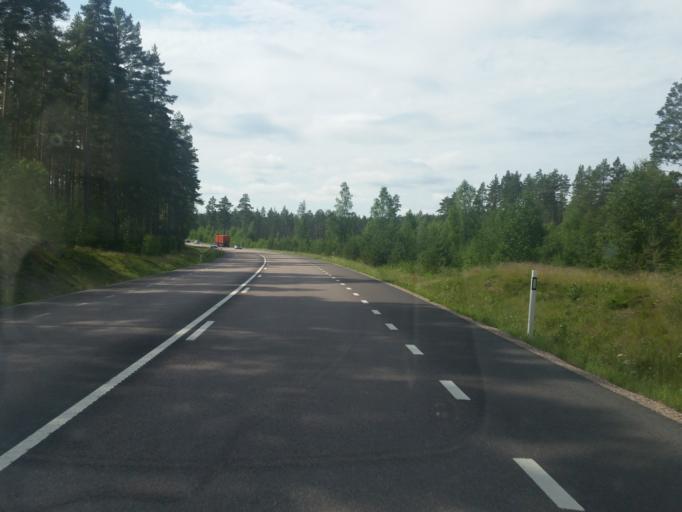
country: SE
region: Dalarna
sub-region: Gagnefs Kommun
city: Gagnef
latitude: 60.6455
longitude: 15.0603
